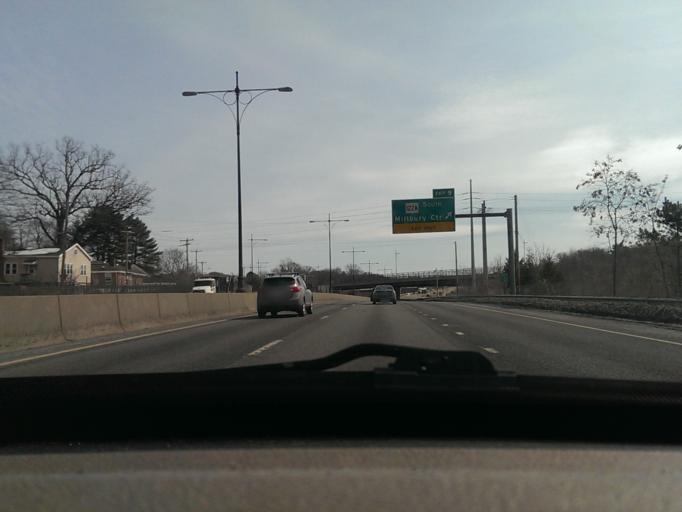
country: US
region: Massachusetts
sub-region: Worcester County
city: Millbury
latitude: 42.2041
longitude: -71.7778
